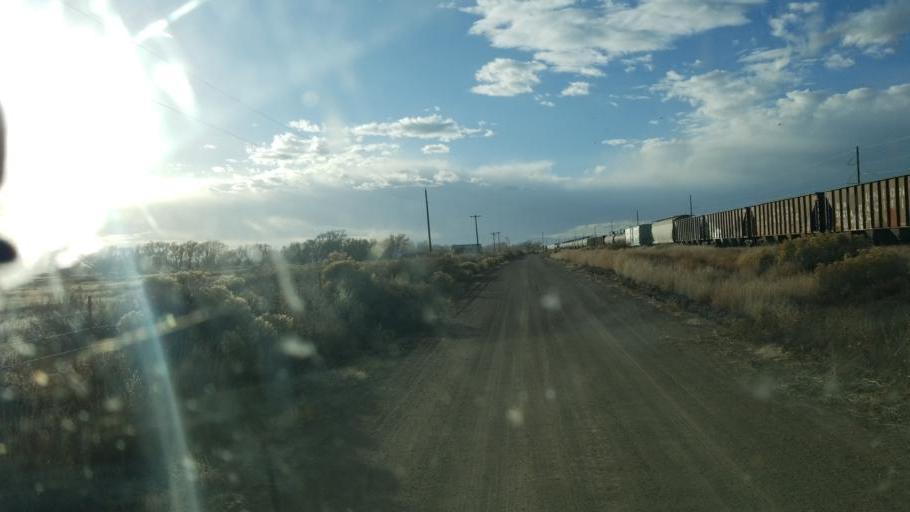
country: US
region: Colorado
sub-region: Alamosa County
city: Alamosa East
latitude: 37.4651
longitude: -105.8354
